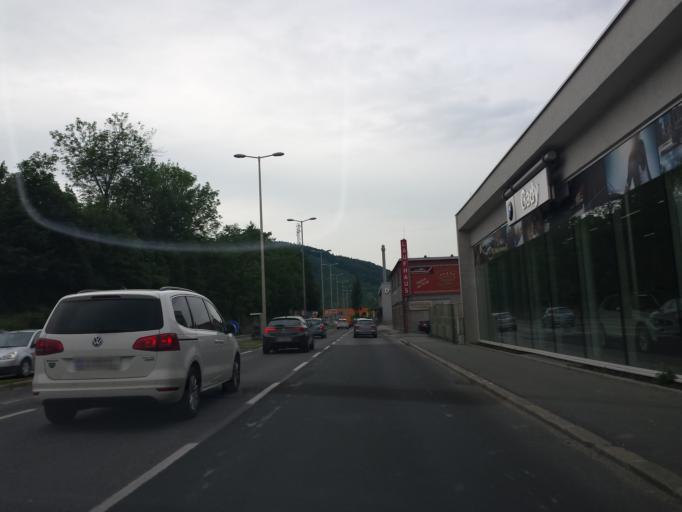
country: AT
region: Styria
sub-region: Graz Stadt
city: Goesting
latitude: 47.0993
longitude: 15.4036
